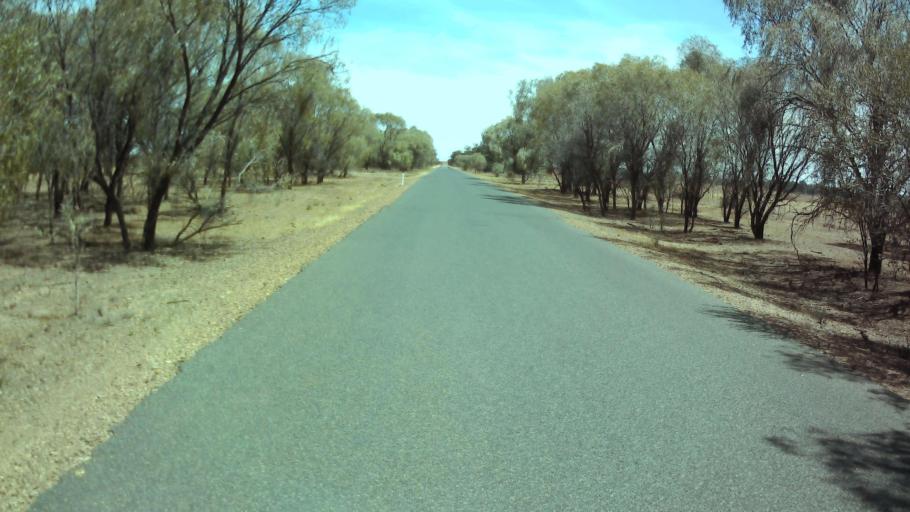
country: AU
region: New South Wales
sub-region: Weddin
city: Grenfell
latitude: -33.8753
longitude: 147.7439
